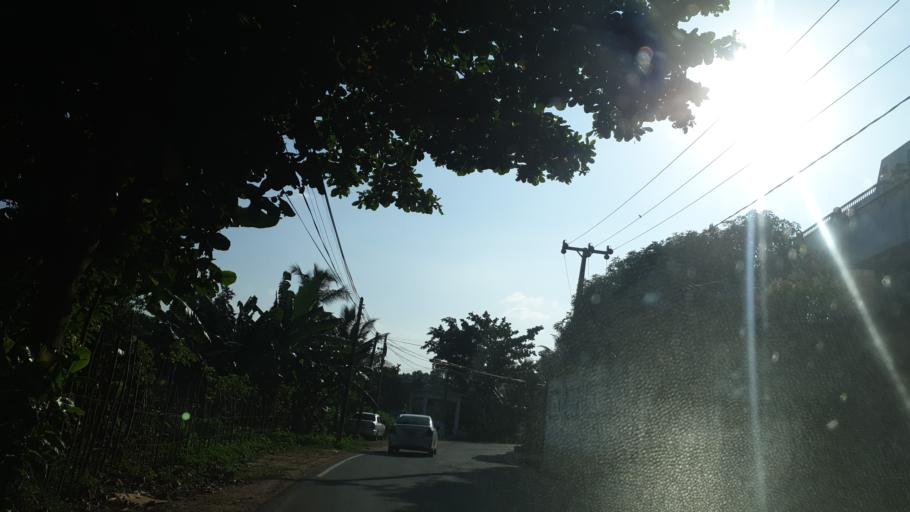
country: LK
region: Western
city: Sri Jayewardenepura Kotte
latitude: 6.8730
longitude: 79.9170
